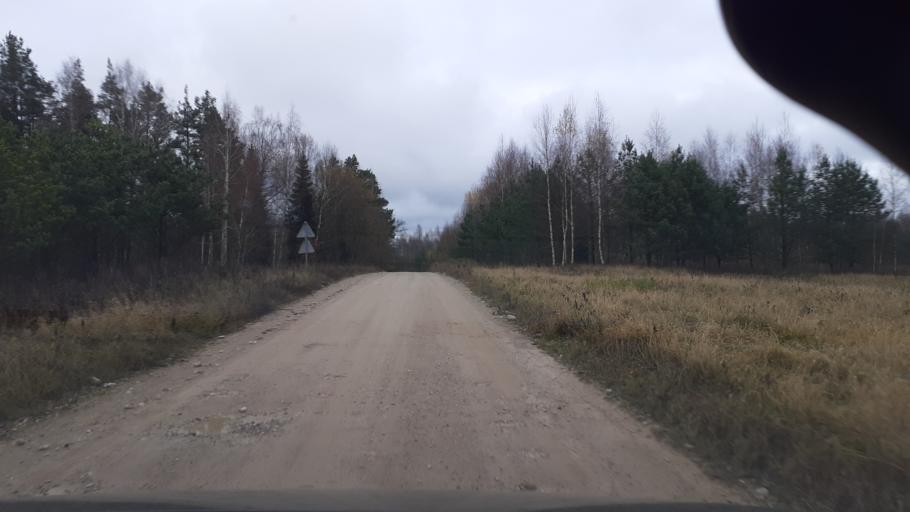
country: LV
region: Kuldigas Rajons
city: Kuldiga
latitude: 57.0352
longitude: 21.8784
